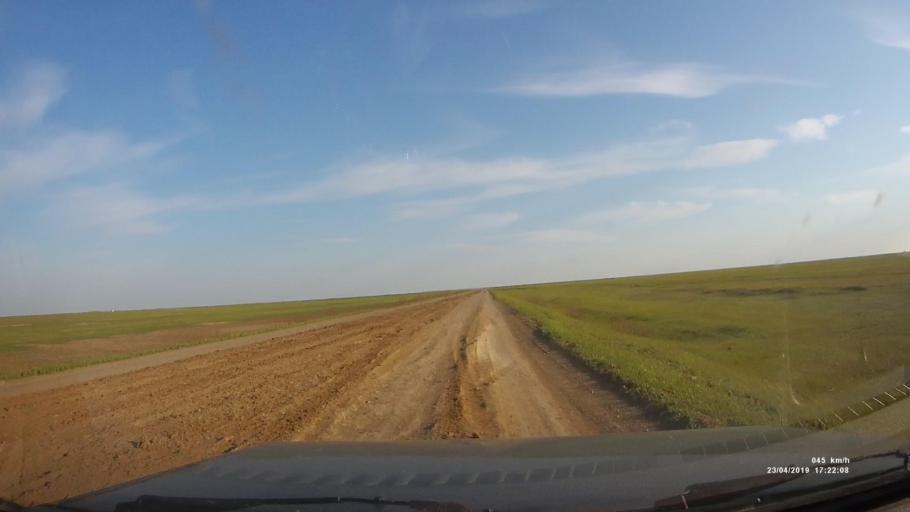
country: RU
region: Kalmykiya
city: Priyutnoye
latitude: 46.1709
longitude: 43.5062
